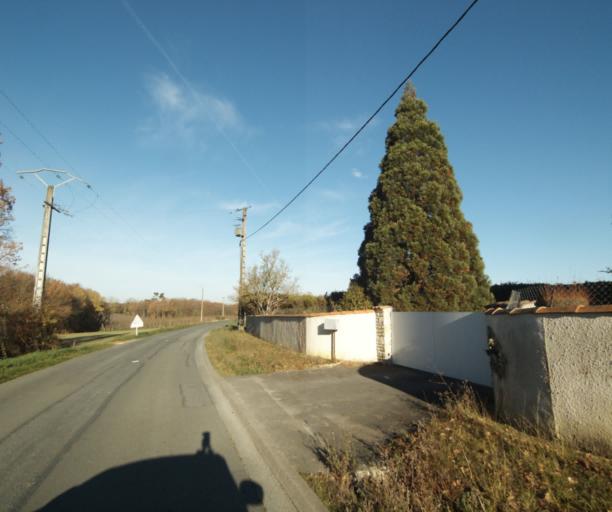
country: FR
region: Poitou-Charentes
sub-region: Departement de la Charente-Maritime
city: Chaniers
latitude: 45.7479
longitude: -0.5635
